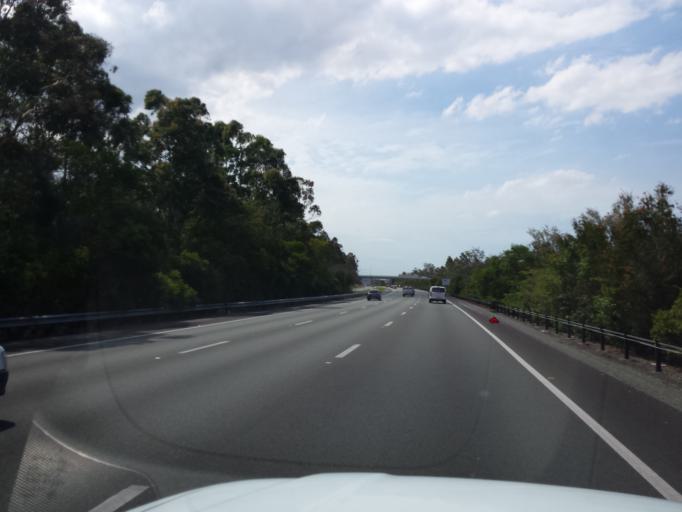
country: AU
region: Queensland
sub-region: Gold Coast
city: Nerang
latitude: -27.9558
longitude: 153.3441
